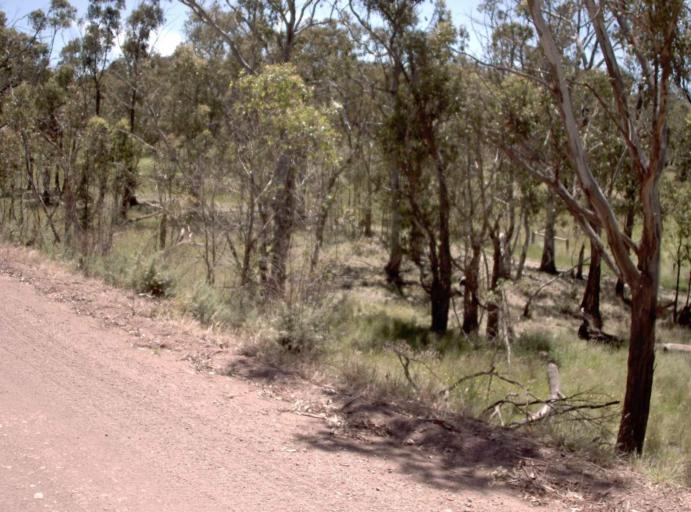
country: AU
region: New South Wales
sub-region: Snowy River
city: Jindabyne
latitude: -37.0337
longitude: 148.2736
